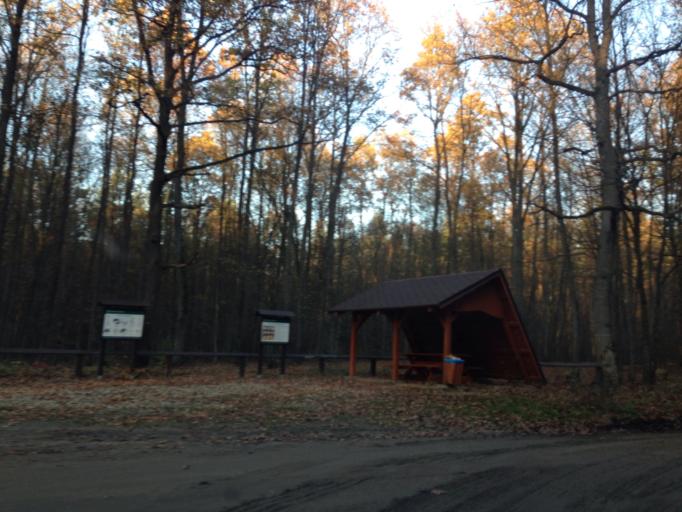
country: PL
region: Kujawsko-Pomorskie
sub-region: Powiat brodnicki
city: Gorzno
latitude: 53.1997
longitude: 19.6934
